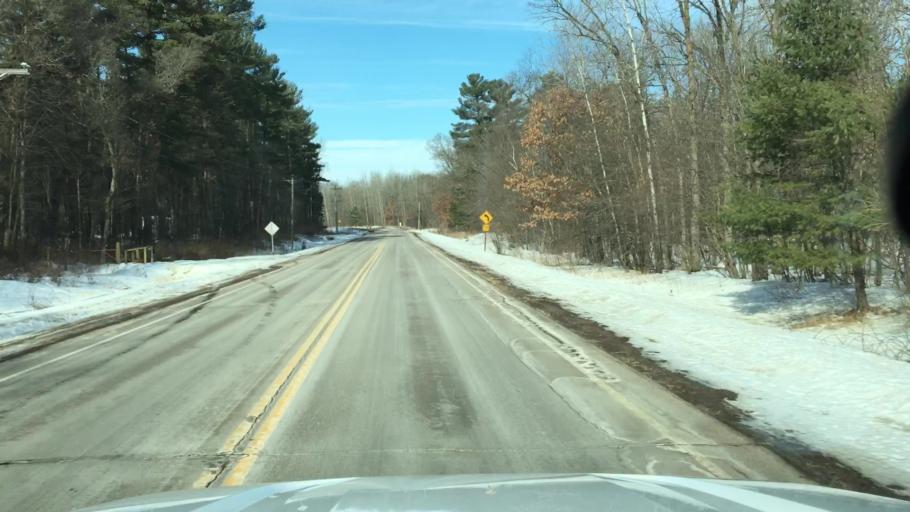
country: US
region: Wisconsin
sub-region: Polk County
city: Saint Croix Falls
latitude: 45.4665
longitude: -92.6869
